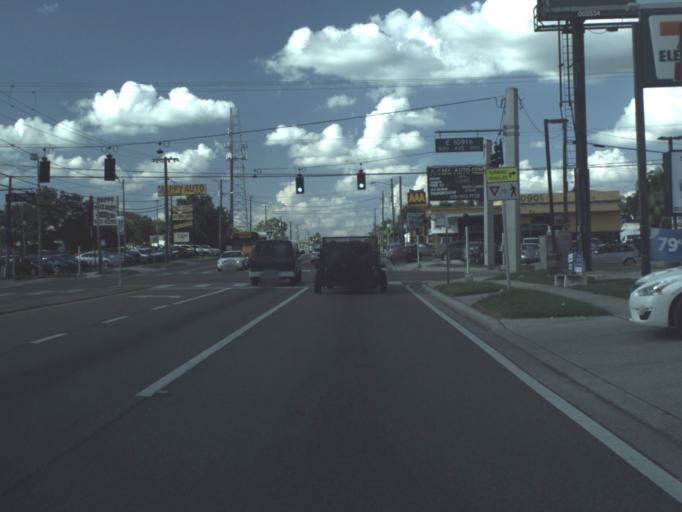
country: US
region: Florida
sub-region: Hillsborough County
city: University
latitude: 28.0467
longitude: -82.4511
